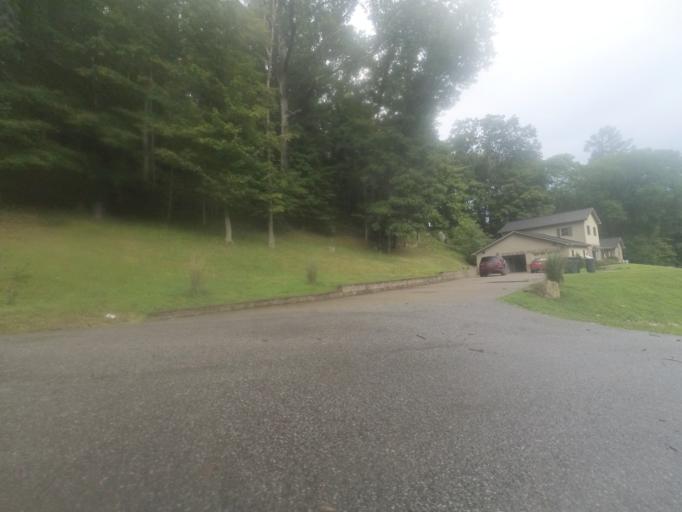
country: US
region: West Virginia
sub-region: Cabell County
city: Huntington
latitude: 38.3868
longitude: -82.4056
